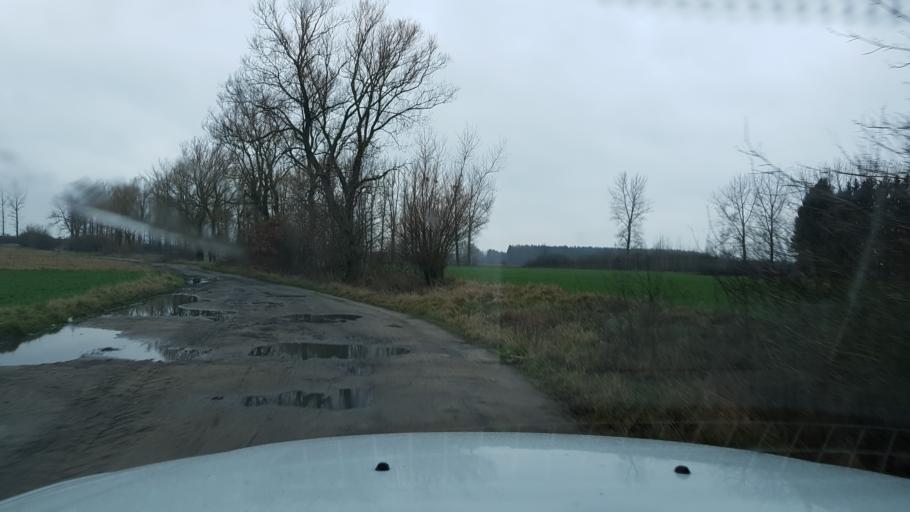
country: PL
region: West Pomeranian Voivodeship
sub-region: Powiat gryficki
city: Brojce
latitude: 53.9879
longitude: 15.3121
